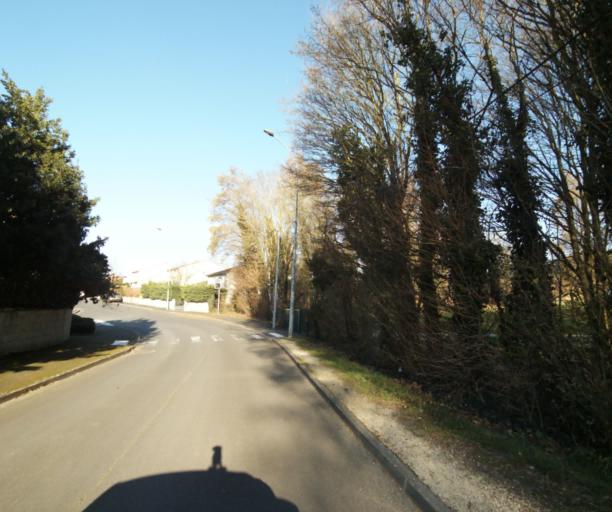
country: FR
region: Poitou-Charentes
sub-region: Departement des Deux-Sevres
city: Niort
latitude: 46.3372
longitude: -0.4386
